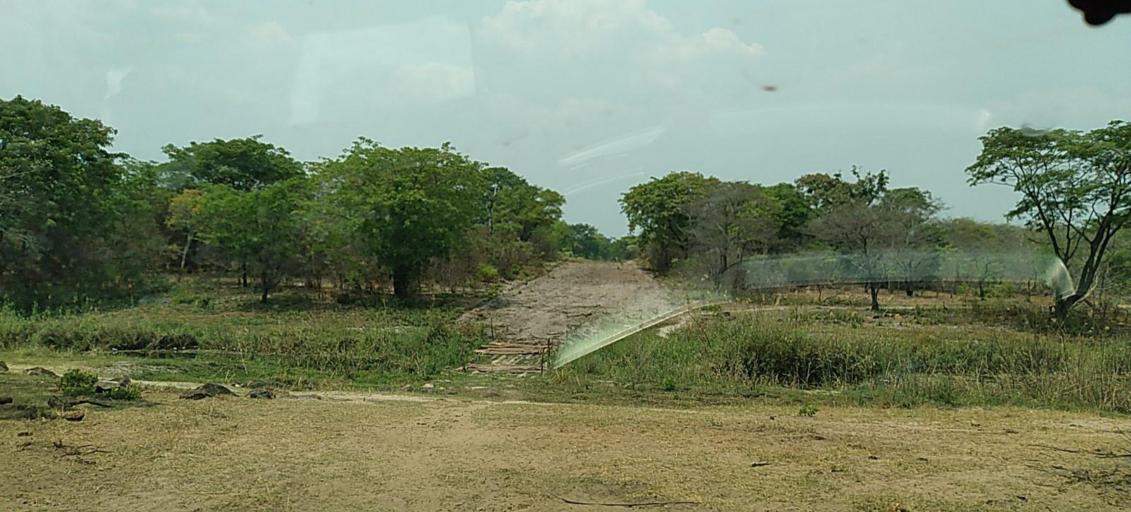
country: ZM
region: Western
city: Lukulu
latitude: -14.0030
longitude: 23.5888
